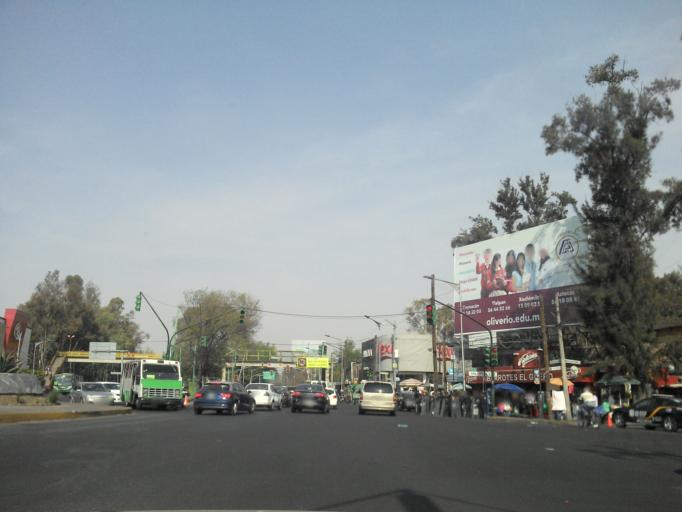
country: MX
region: Mexico City
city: Tlalpan
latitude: 19.2978
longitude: -99.1518
